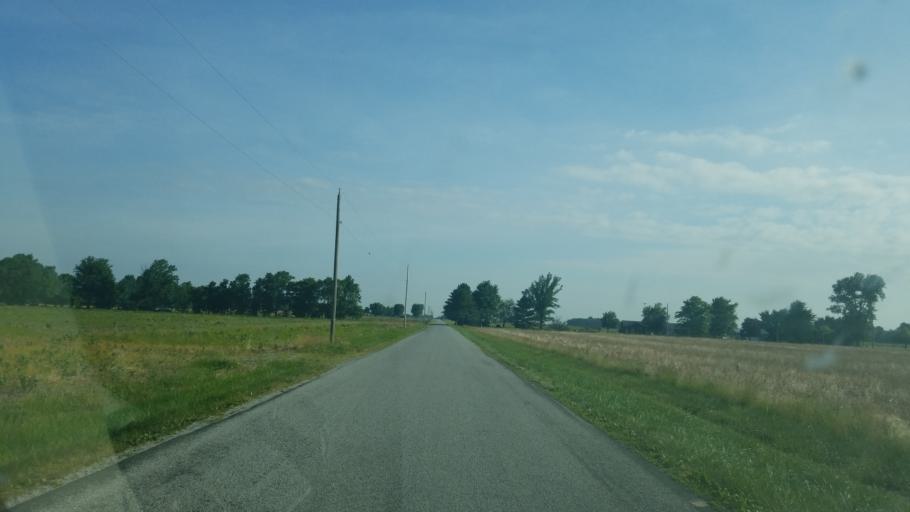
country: US
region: Ohio
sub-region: Hancock County
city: Arlington
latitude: 40.8031
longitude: -83.6706
